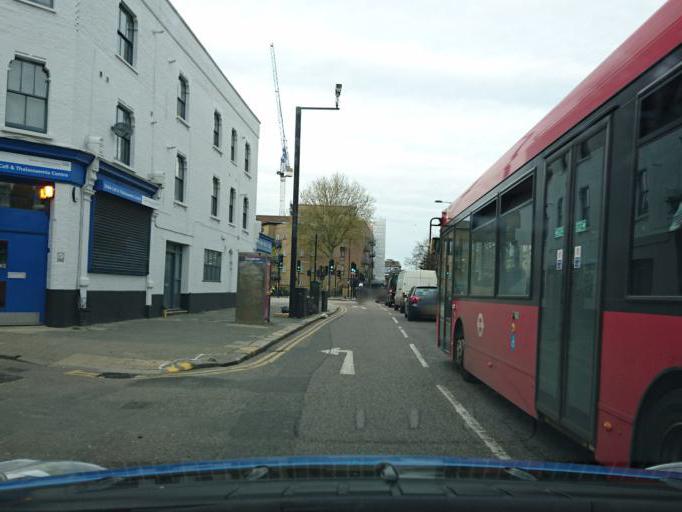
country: GB
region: England
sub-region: Greater London
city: Hackney
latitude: 51.5457
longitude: -0.0698
